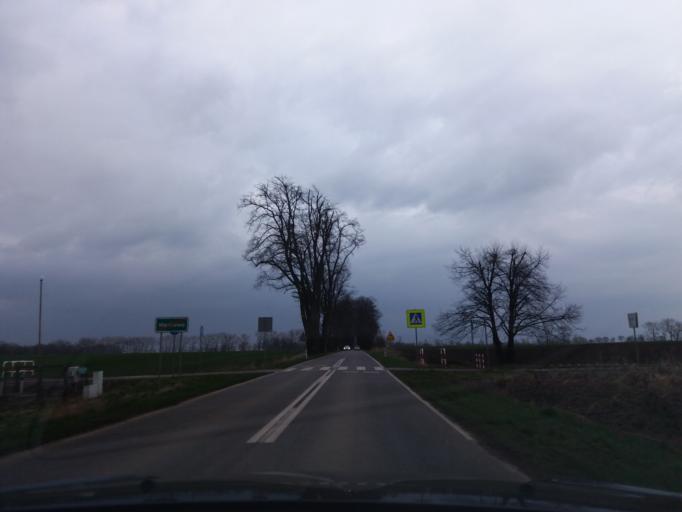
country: PL
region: West Pomeranian Voivodeship
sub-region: Powiat pyrzycki
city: Pyrzyce
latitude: 53.1372
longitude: 14.9709
